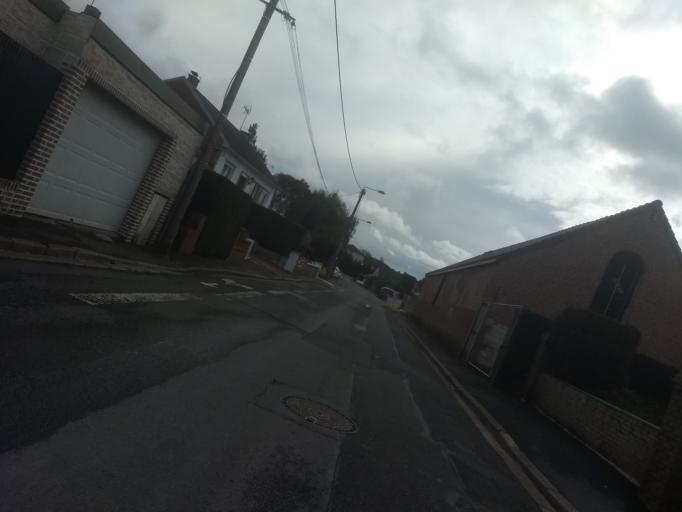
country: FR
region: Nord-Pas-de-Calais
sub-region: Departement du Pas-de-Calais
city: Anzin-Saint-Aubin
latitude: 50.3088
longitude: 2.7503
